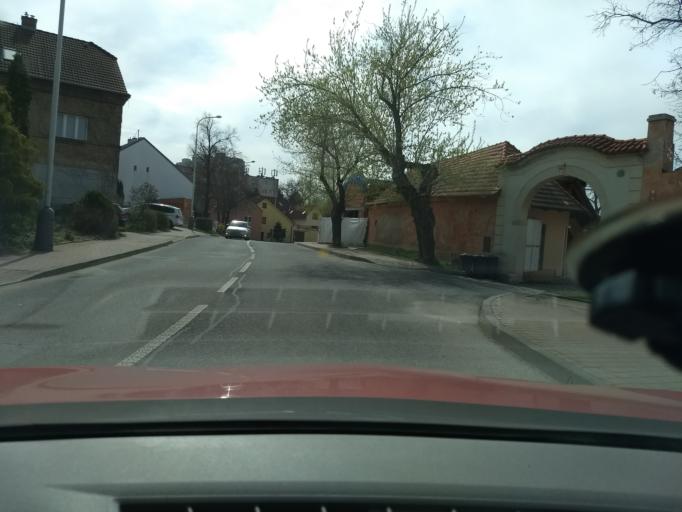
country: CZ
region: Central Bohemia
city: Hostivice
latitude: 50.0709
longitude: 14.3001
